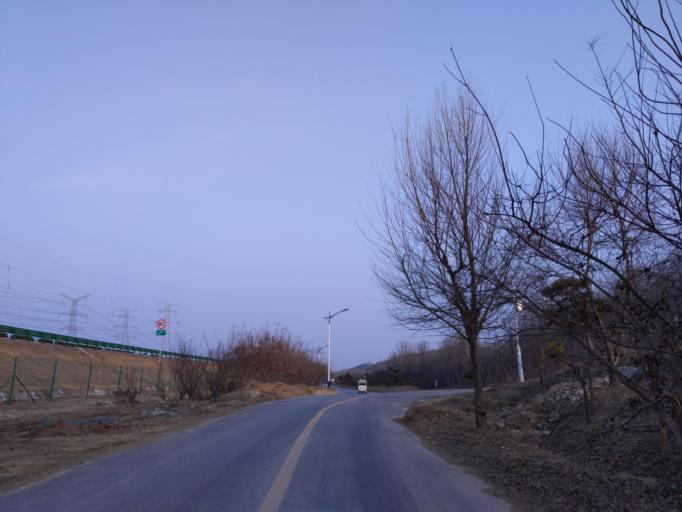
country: CN
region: Henan Sheng
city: Puyang
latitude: 35.8209
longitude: 115.0197
